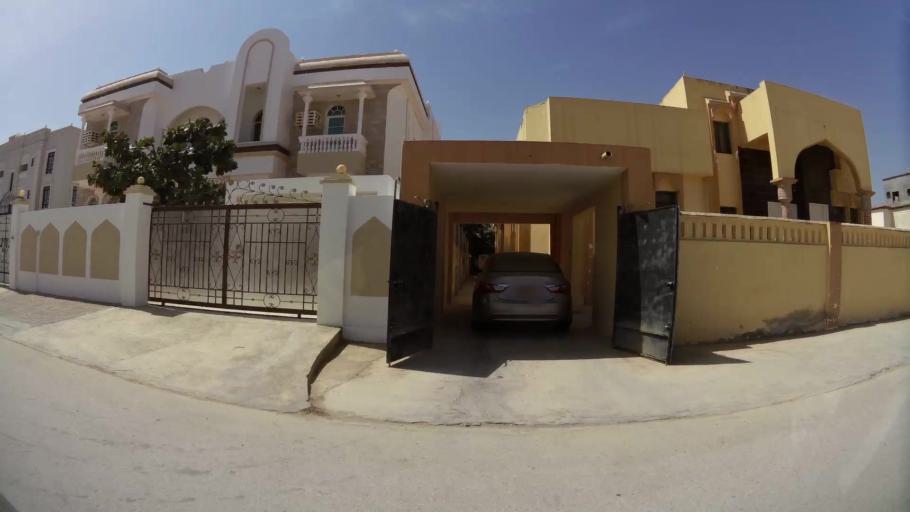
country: OM
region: Zufar
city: Salalah
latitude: 17.0427
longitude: 54.1499
